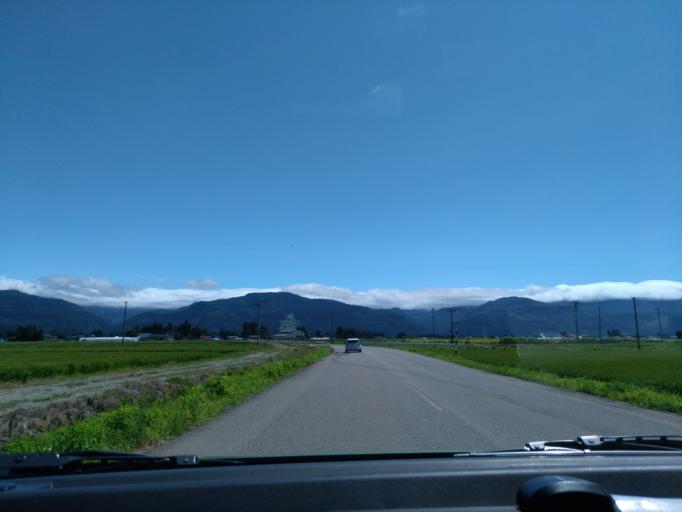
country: JP
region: Akita
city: Kakunodatemachi
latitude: 39.5308
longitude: 140.5937
